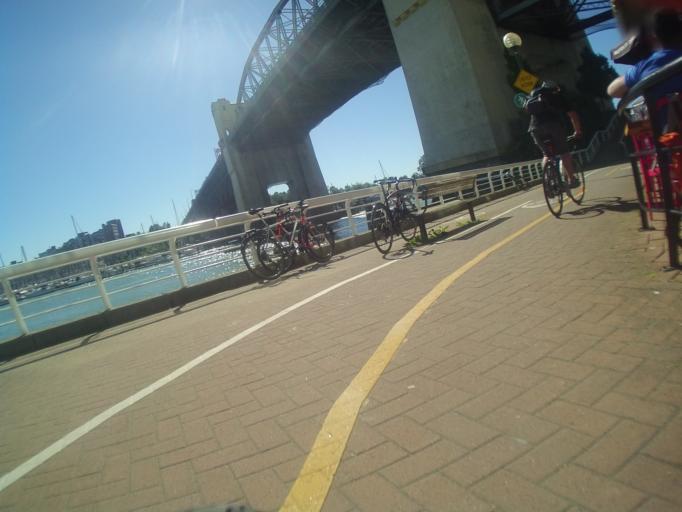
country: CA
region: British Columbia
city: West End
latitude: 49.2754
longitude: -123.1355
